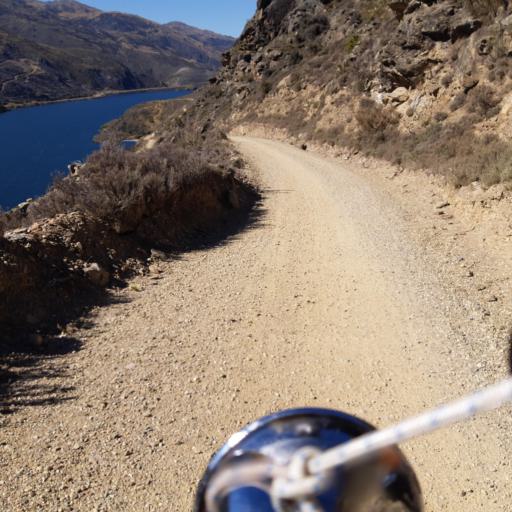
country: NZ
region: Otago
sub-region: Queenstown-Lakes District
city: Wanaka
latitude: -45.0863
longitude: 169.2555
